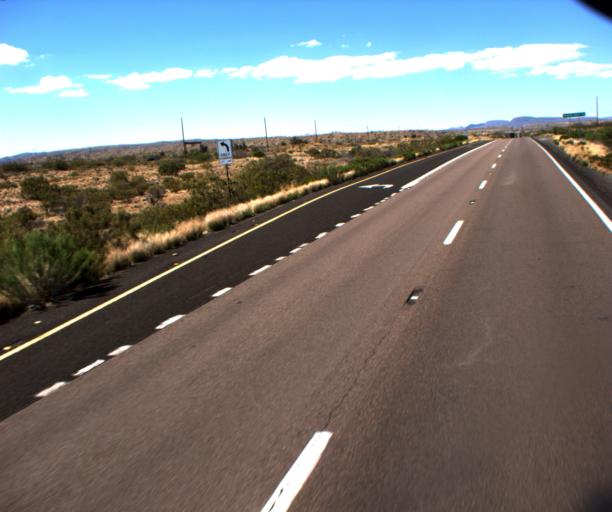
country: US
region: Arizona
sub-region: Mohave County
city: Kingman
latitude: 35.0272
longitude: -113.6642
